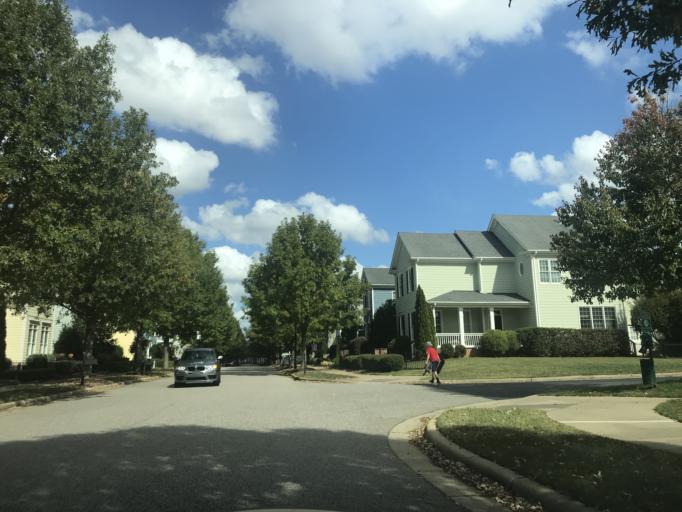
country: US
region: North Carolina
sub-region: Wake County
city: Raleigh
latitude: 35.7348
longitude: -78.6558
